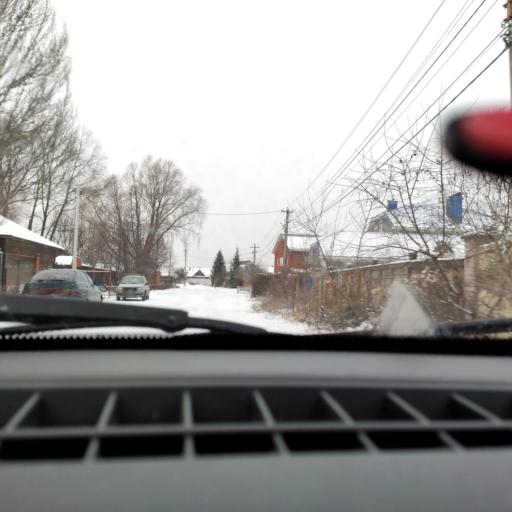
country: RU
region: Bashkortostan
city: Ufa
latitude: 54.6181
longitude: 55.9128
